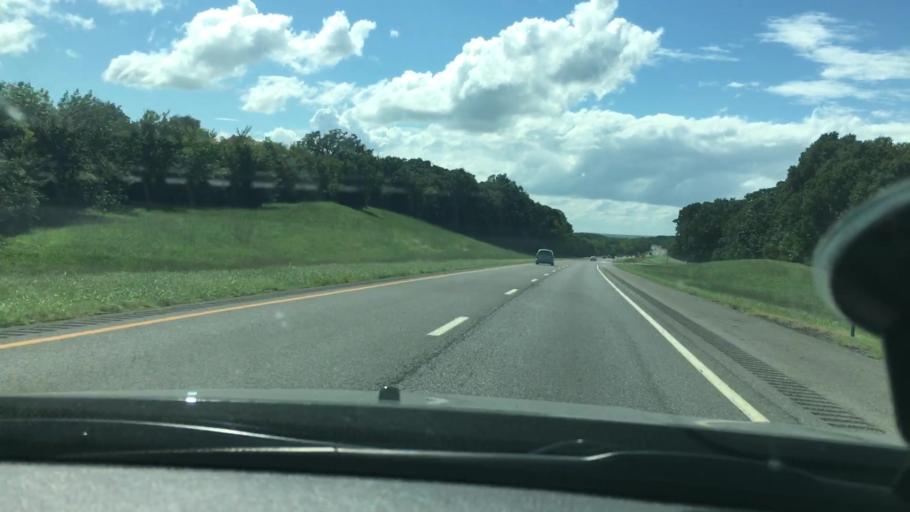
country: US
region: Oklahoma
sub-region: Sequoyah County
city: Vian
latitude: 35.4904
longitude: -95.0705
